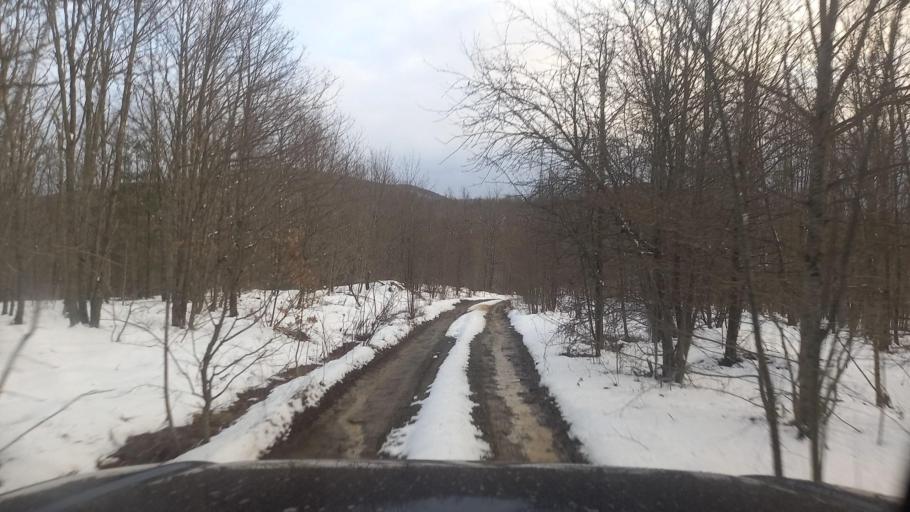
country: RU
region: Krasnodarskiy
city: Smolenskaya
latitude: 44.6802
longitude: 38.7672
